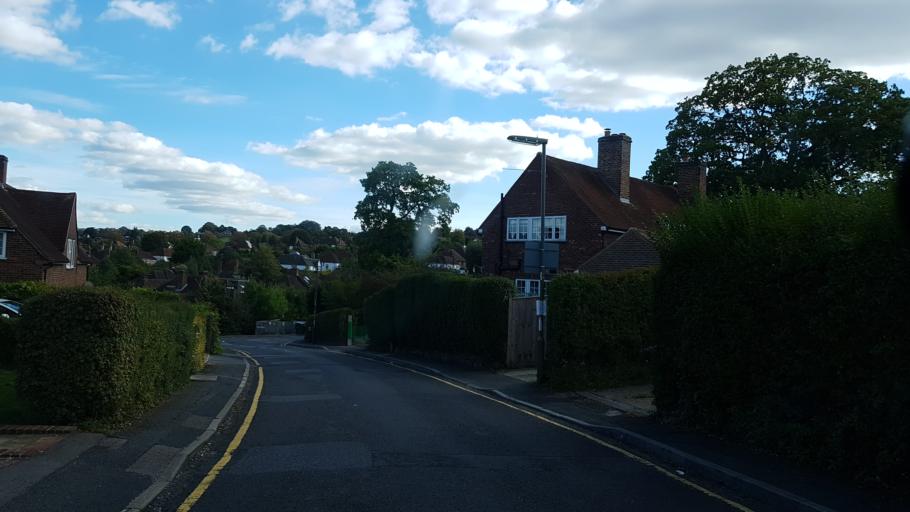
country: GB
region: England
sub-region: Surrey
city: Guildford
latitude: 51.2372
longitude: -0.5944
